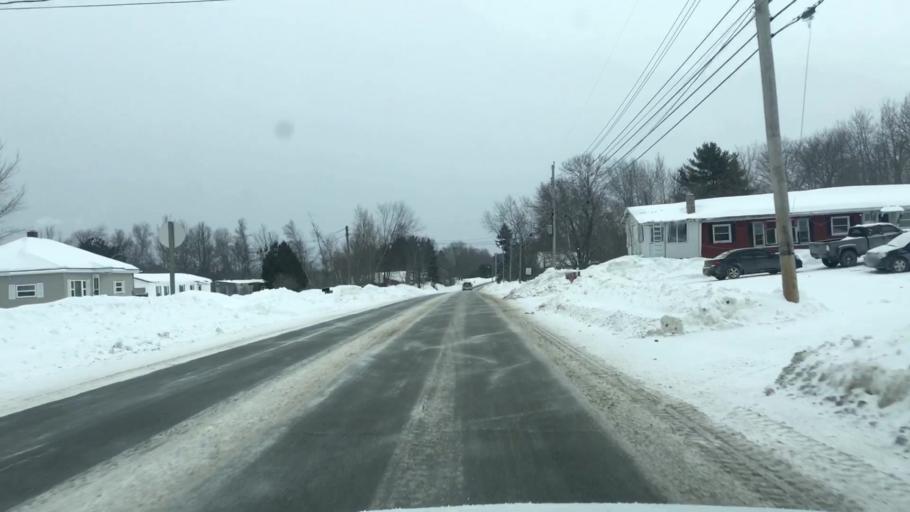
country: US
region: Maine
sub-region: Penobscot County
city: Lincoln
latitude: 45.3986
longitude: -68.4916
